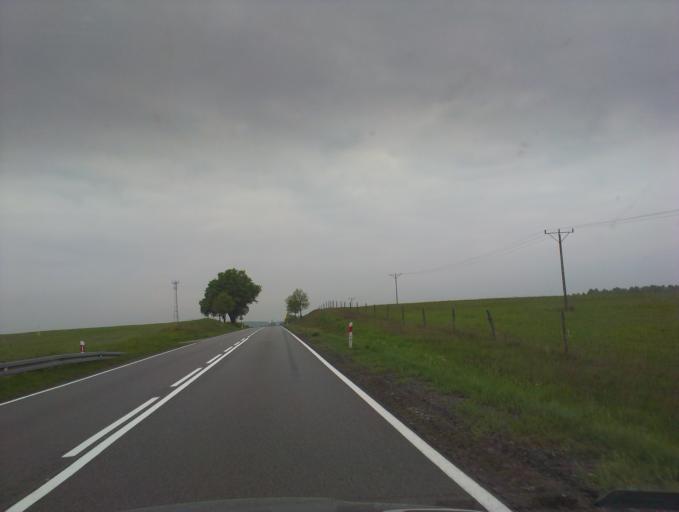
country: PL
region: West Pomeranian Voivodeship
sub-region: Powiat koszalinski
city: Bobolice
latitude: 53.8496
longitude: 16.6187
